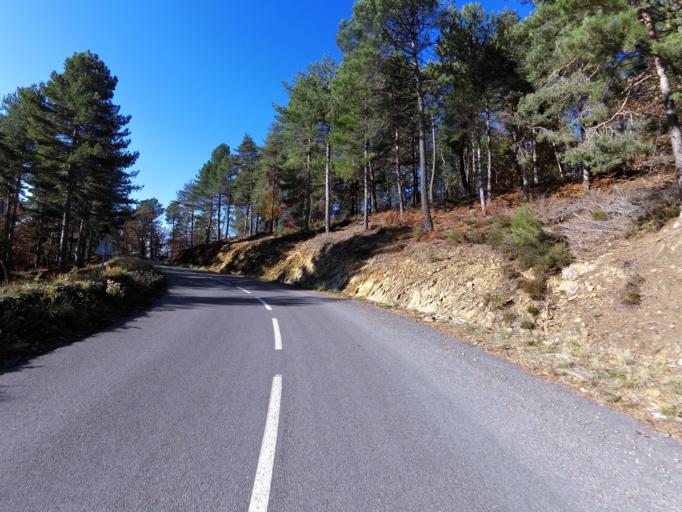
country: FR
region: Rhone-Alpes
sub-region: Departement de l'Ardeche
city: Les Vans
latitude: 44.4997
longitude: 4.1268
